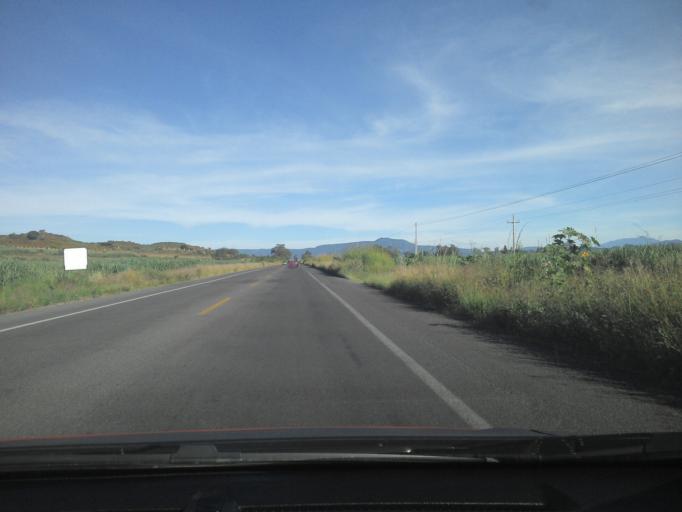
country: MX
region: Jalisco
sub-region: Teuchitlan
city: La Estanzuela
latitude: 20.6684
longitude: -103.7968
